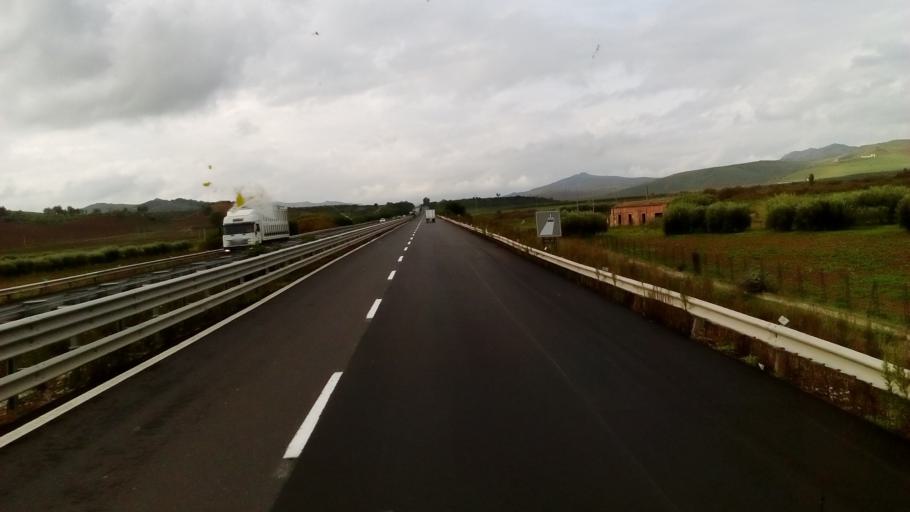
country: IT
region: Sicily
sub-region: Enna
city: Catenanuova
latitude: 37.5674
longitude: 14.6353
